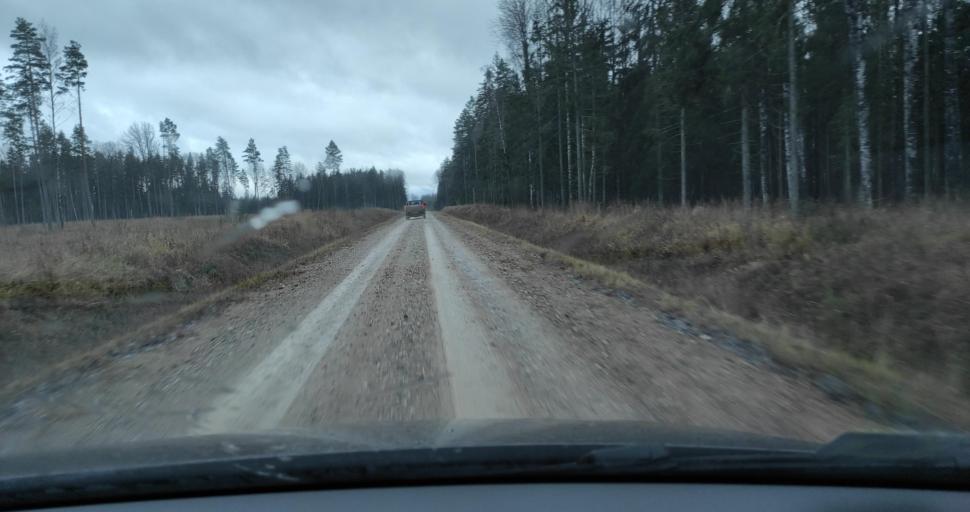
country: LV
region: Skrunda
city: Skrunda
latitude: 56.5604
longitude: 22.0800
